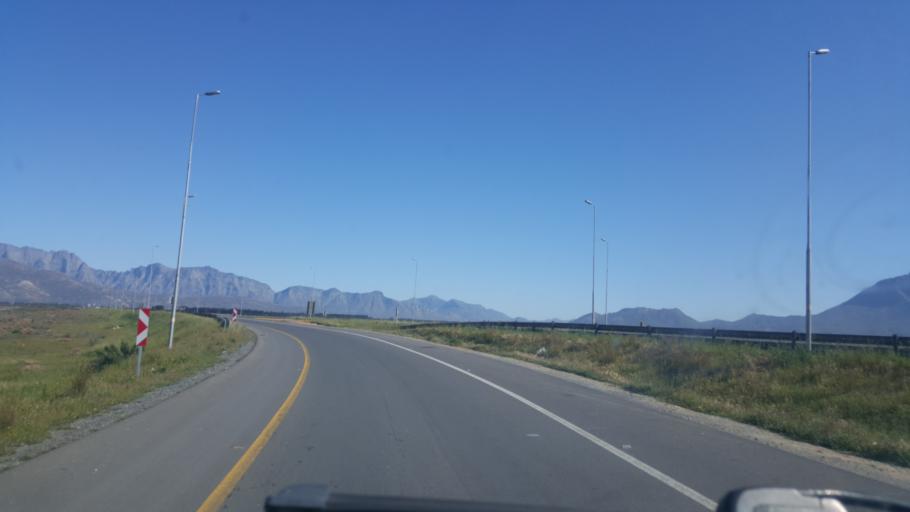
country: ZA
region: Western Cape
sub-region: Cape Winelands District Municipality
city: Worcester
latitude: -33.6348
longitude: 19.3574
